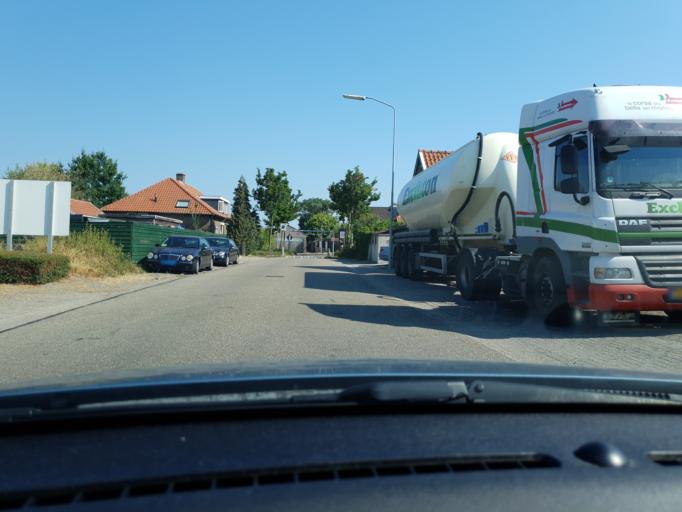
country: NL
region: Gelderland
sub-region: Gemeente Nijmegen
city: Lindenholt
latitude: 51.8521
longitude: 5.8141
